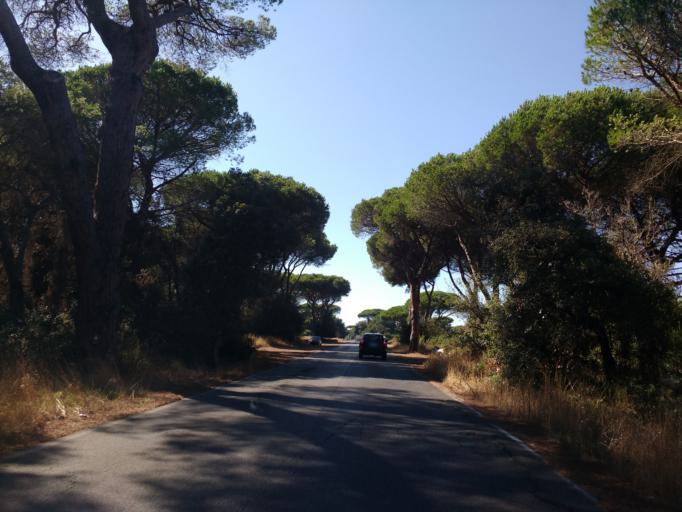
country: IT
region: Latium
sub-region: Citta metropolitana di Roma Capitale
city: Acilia-Castel Fusano-Ostia Antica
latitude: 41.7124
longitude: 12.3576
